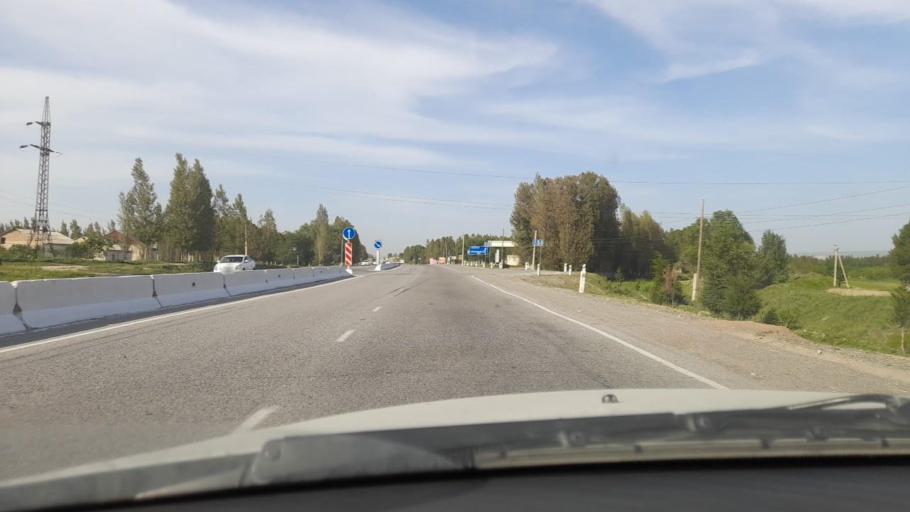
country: UZ
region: Jizzax
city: Jizzax
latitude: 39.9601
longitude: 67.5459
